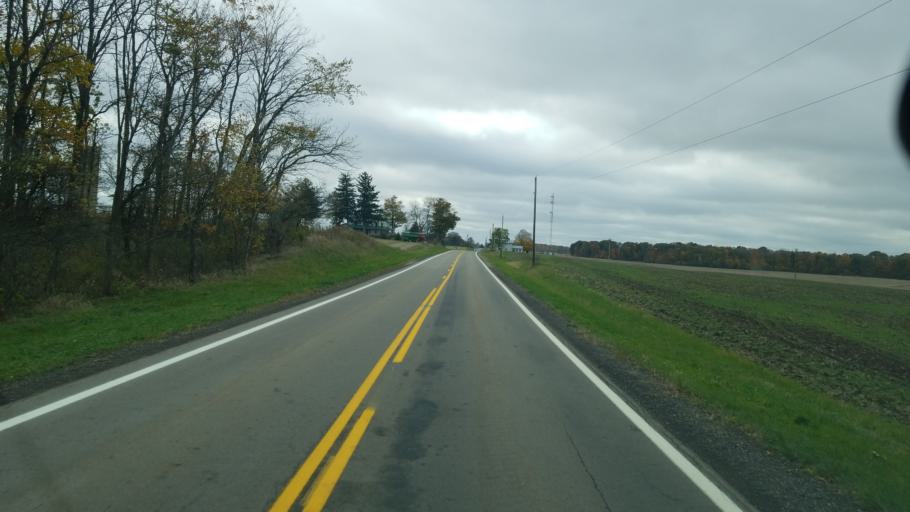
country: US
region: Ohio
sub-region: Richland County
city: Shelby
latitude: 40.9020
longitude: -82.7410
